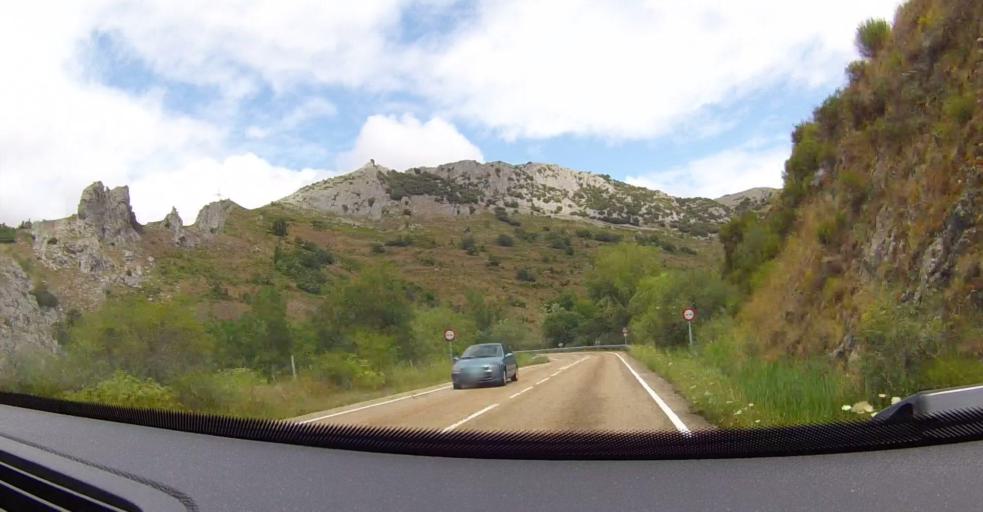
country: ES
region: Castille and Leon
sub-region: Provincia de Leon
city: Puebla de Lillo
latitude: 42.9594
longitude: -5.2510
